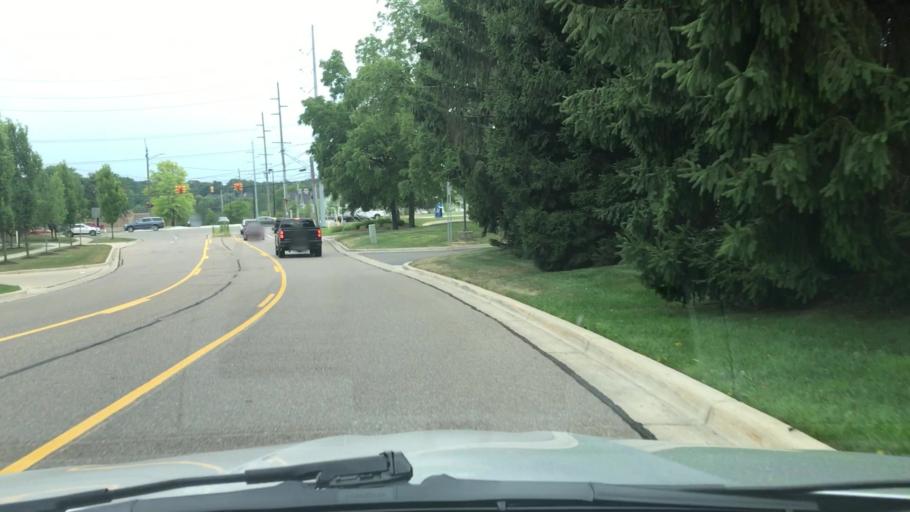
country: US
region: Michigan
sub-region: Wayne County
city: Northville
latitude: 42.4399
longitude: -83.4389
